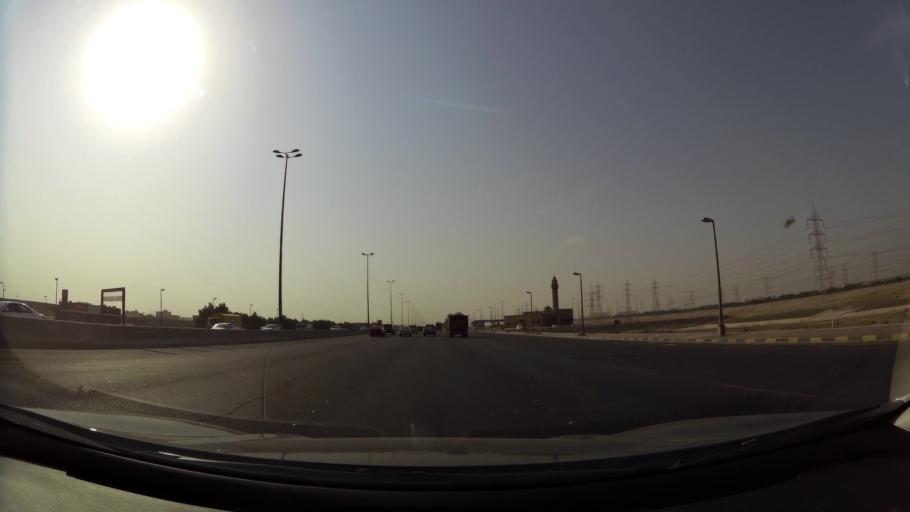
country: KW
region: Al Ahmadi
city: Ar Riqqah
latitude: 29.1176
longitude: 48.0938
